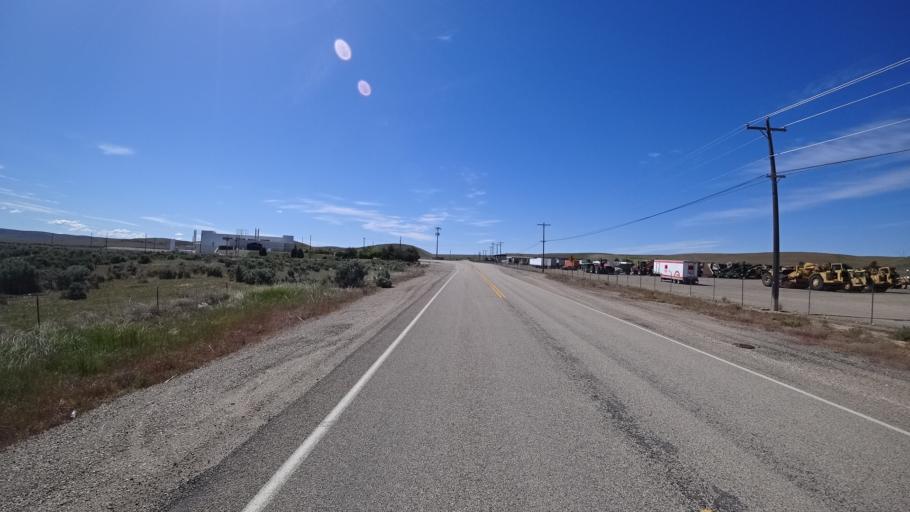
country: US
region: Idaho
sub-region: Ada County
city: Boise
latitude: 43.5141
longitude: -116.1437
